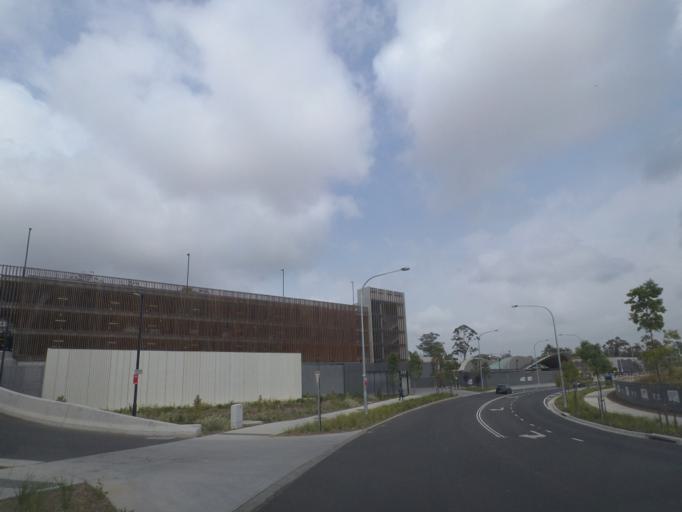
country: AU
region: New South Wales
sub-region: The Hills Shire
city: West Pennant
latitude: -33.7370
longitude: 151.0337
